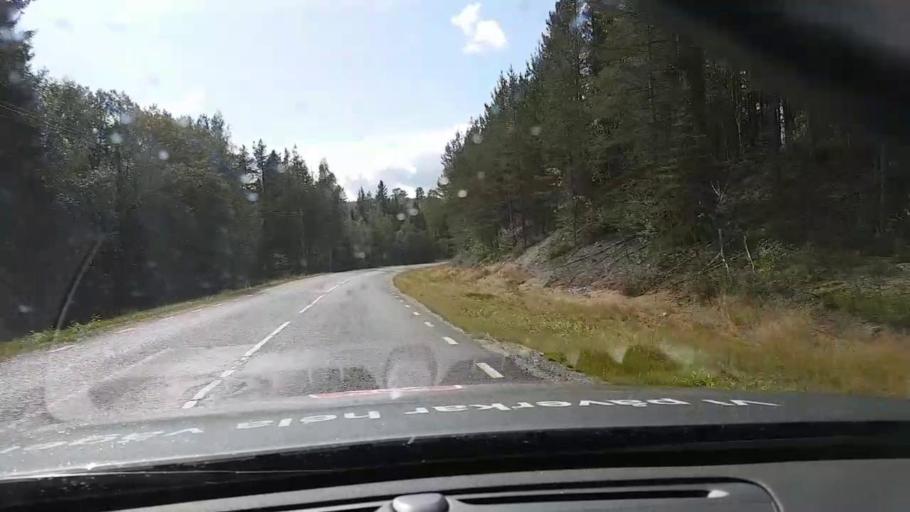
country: SE
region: Vaesterbotten
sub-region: Asele Kommun
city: Asele
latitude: 63.7896
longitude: 17.6004
